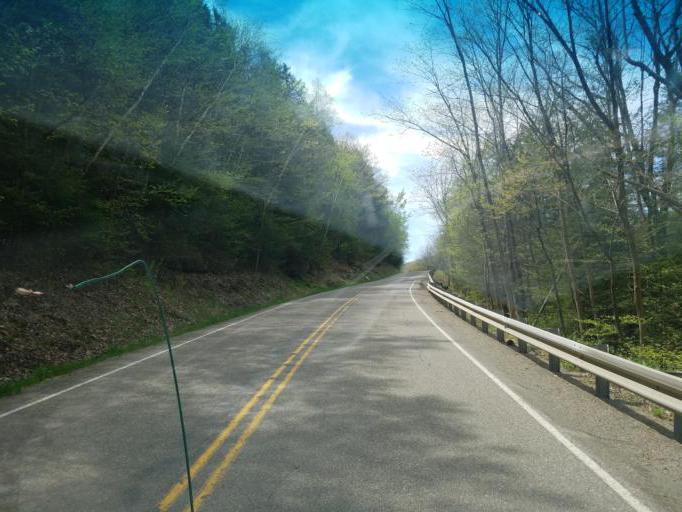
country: US
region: Pennsylvania
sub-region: Tioga County
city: Wellsboro
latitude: 41.7435
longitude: -77.4272
